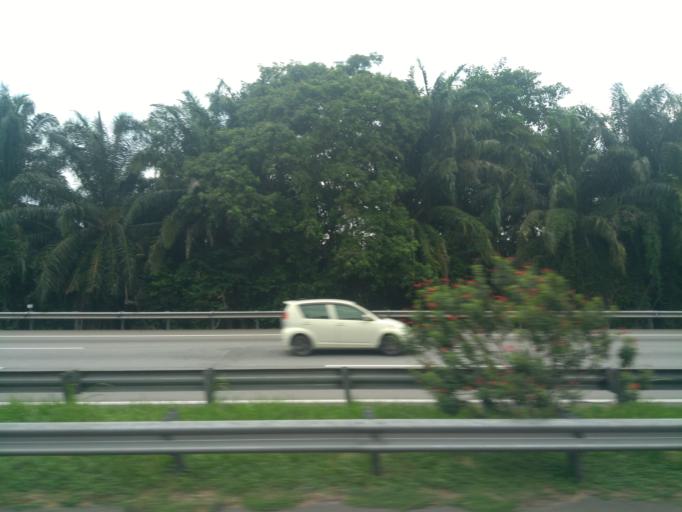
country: MY
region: Melaka
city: Alor Gajah
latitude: 2.3848
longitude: 102.2295
